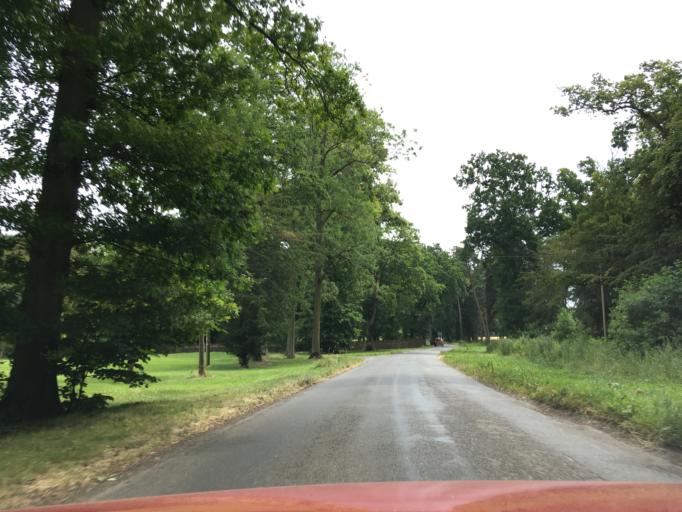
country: GB
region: England
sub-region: Oxfordshire
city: Hook Norton
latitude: 51.9552
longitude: -1.4236
